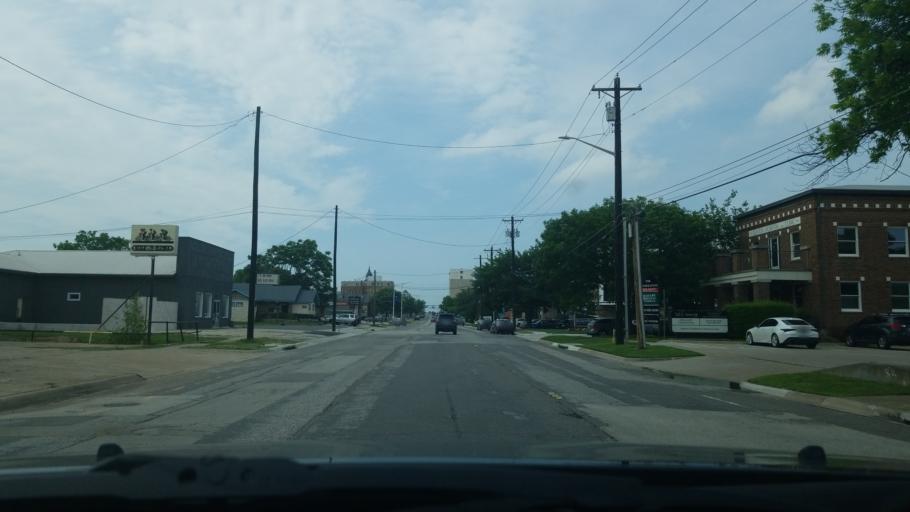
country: US
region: Texas
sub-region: Denton County
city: Denton
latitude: 33.2093
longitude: -97.1325
